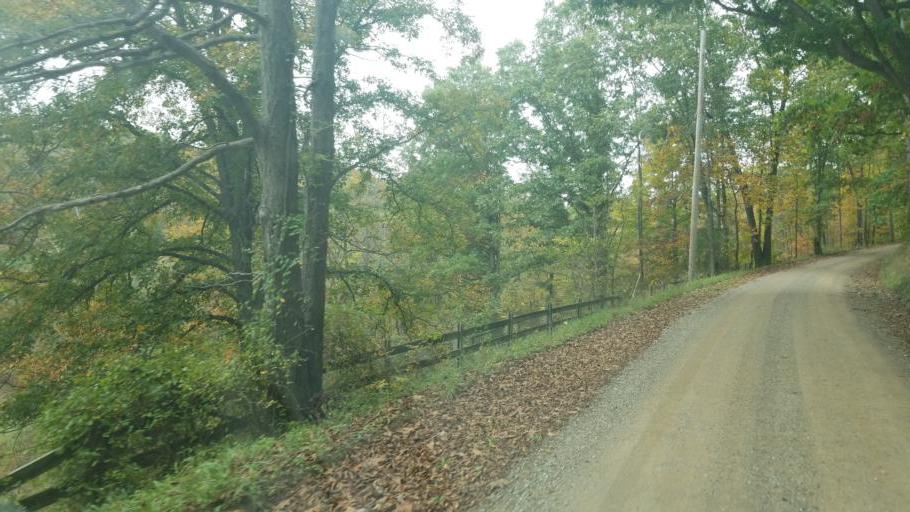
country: US
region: Ohio
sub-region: Wayne County
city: Shreve
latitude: 40.5329
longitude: -82.0854
